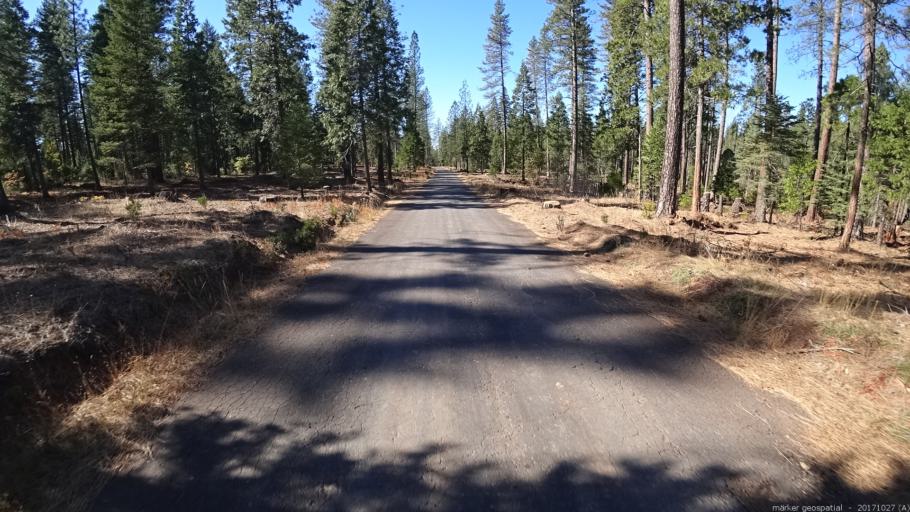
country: US
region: California
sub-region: Shasta County
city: Shingletown
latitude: 40.6221
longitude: -121.8427
